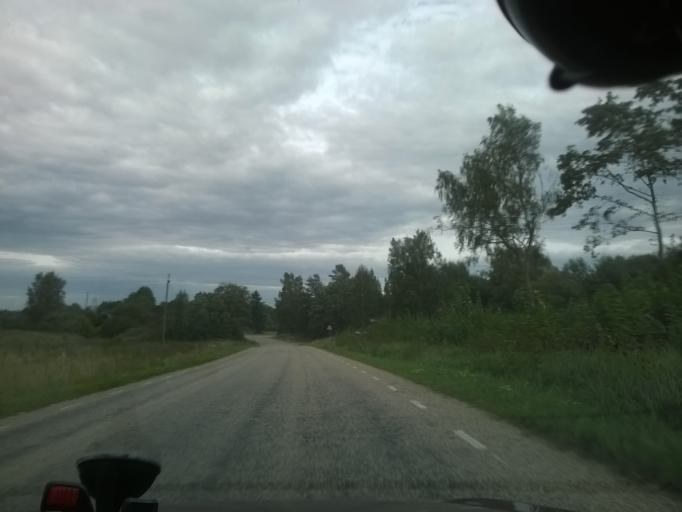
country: EE
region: Vorumaa
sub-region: Voru linn
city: Voru
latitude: 57.7797
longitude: 27.0288
